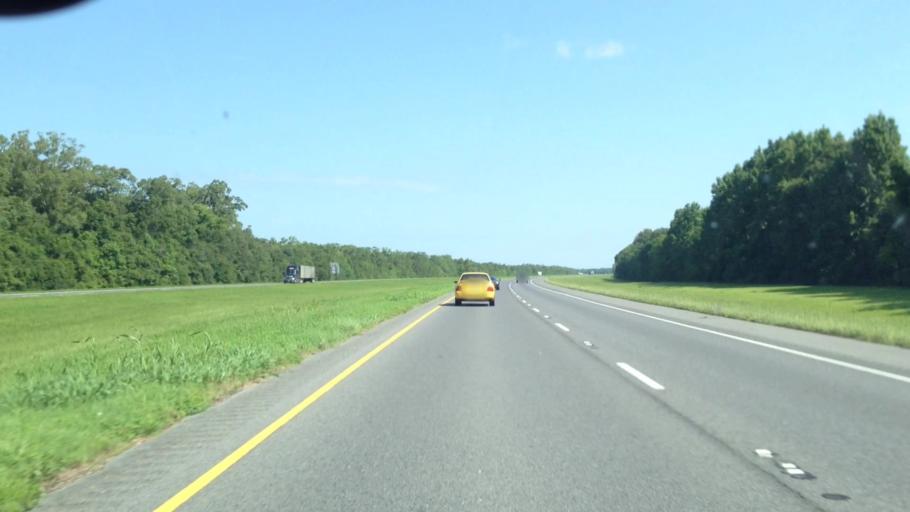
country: US
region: Louisiana
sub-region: Saint Landry Parish
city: Opelousas
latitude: 30.6666
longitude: -92.0700
